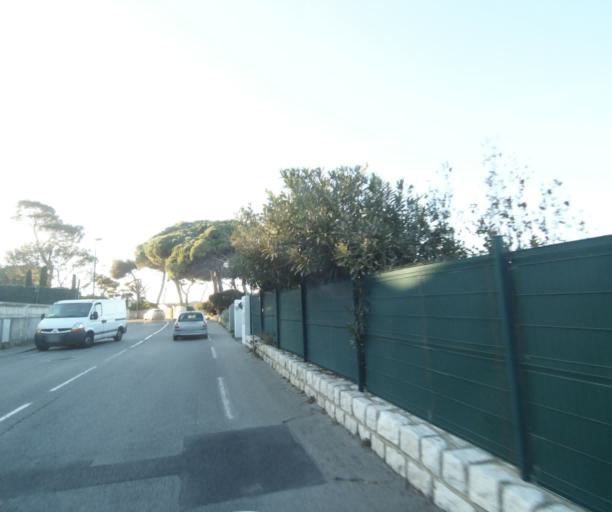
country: FR
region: Provence-Alpes-Cote d'Azur
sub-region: Departement des Alpes-Maritimes
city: Antibes
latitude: 43.5699
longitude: 7.1342
